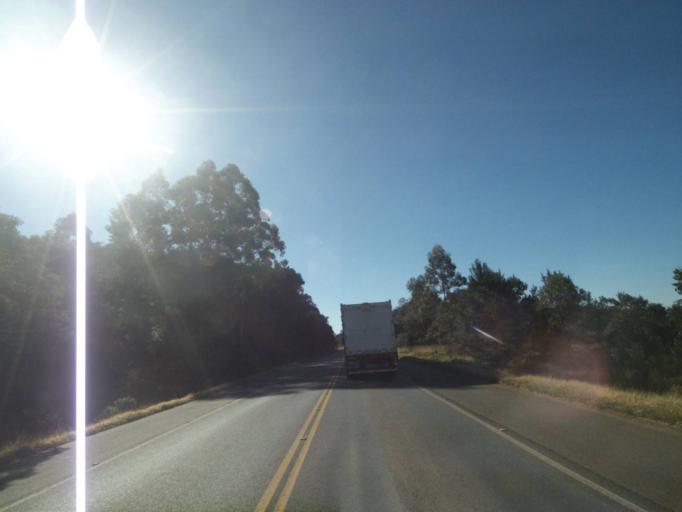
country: BR
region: Parana
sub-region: Tibagi
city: Tibagi
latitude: -24.5621
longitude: -50.4547
